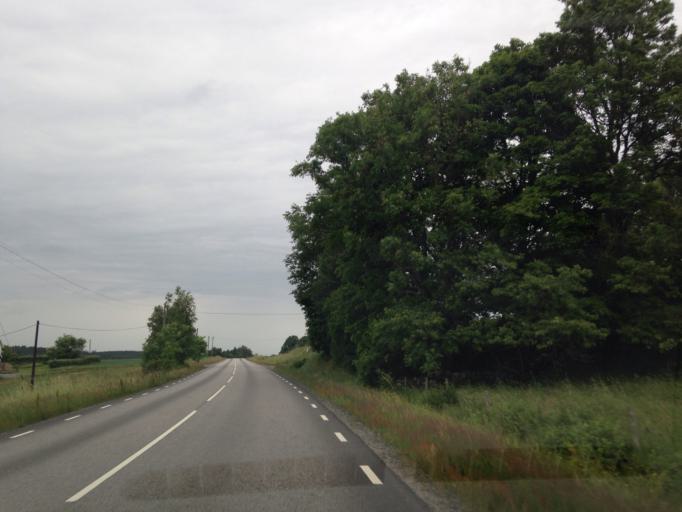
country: SE
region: Vaestra Goetaland
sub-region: Marks Kommun
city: Horred
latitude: 57.4846
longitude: 12.5226
